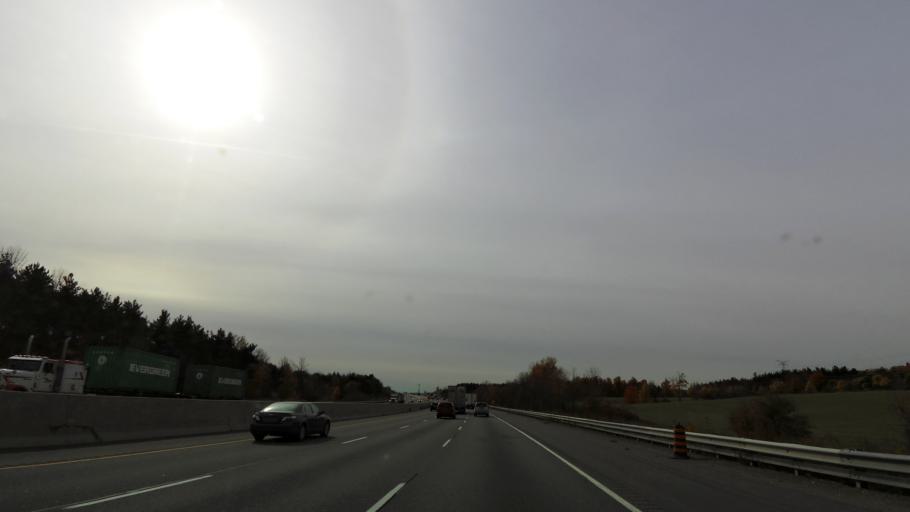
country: CA
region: Ontario
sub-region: Halton
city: Milton
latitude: 43.5113
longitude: -79.9507
